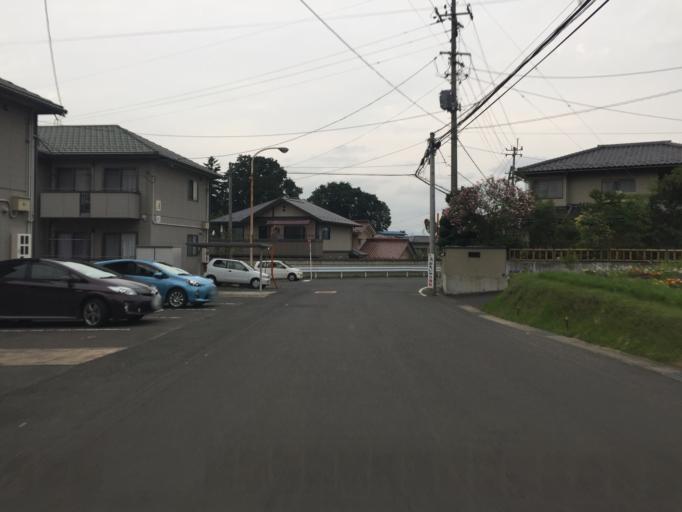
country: JP
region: Fukushima
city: Fukushima-shi
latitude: 37.7207
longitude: 140.4579
